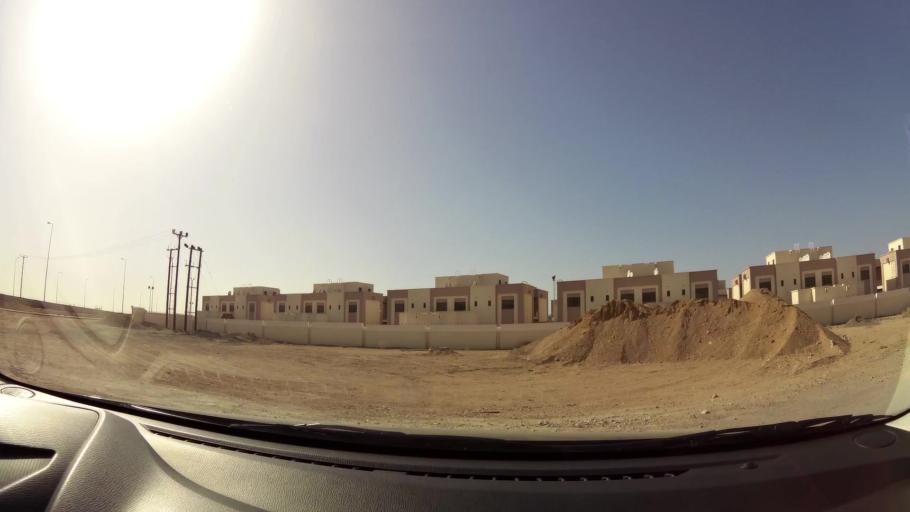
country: OM
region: Muhafazat Masqat
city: Bawshar
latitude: 23.5785
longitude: 58.2761
